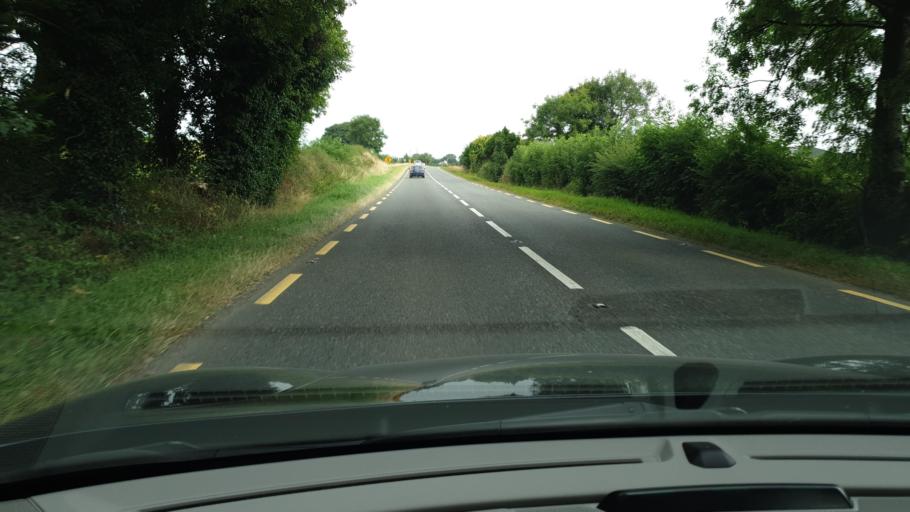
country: IE
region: Leinster
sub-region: An Mhi
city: Athboy
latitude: 53.6900
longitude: -6.9505
